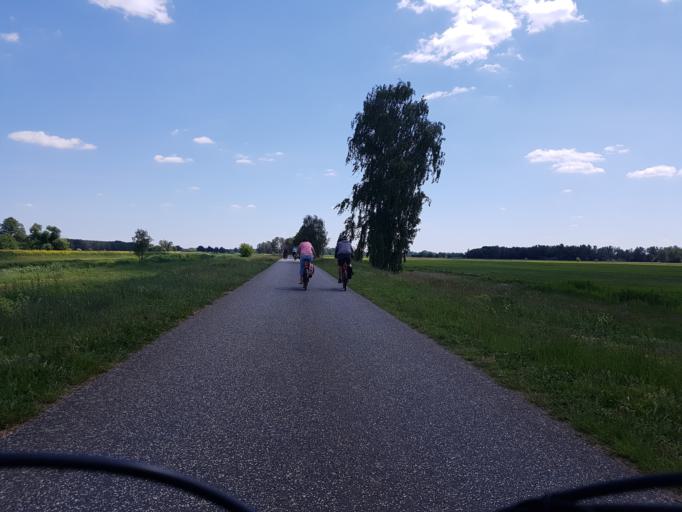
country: DE
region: Brandenburg
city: Bad Liebenwerda
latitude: 51.5394
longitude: 13.3685
